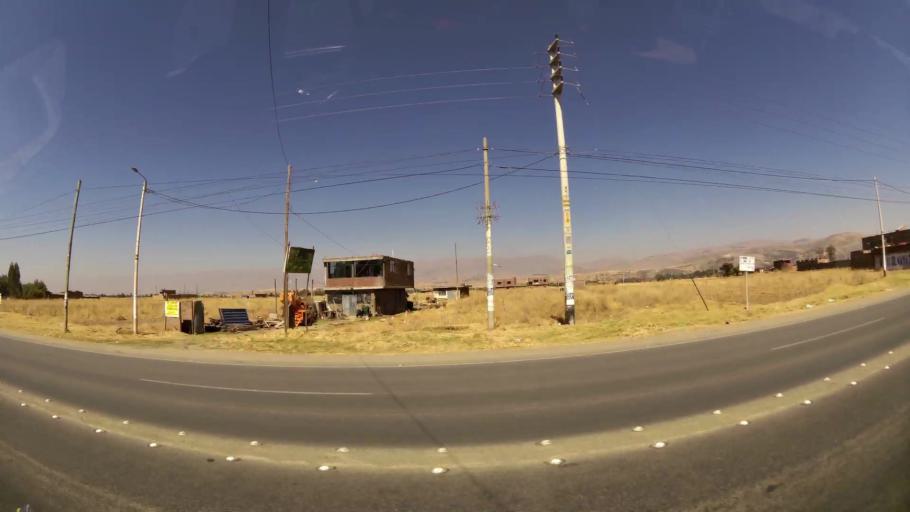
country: PE
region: Junin
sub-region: Provincia de Huancayo
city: San Jeronimo
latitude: -11.9551
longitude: -75.2784
